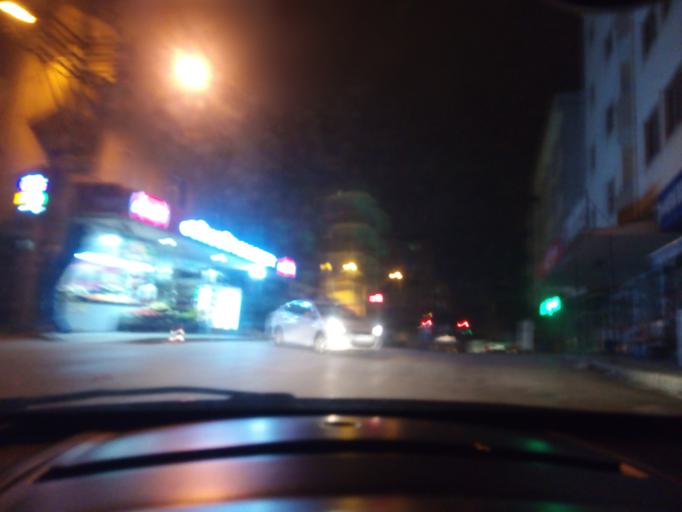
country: TR
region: Bursa
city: Niluefer
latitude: 40.2589
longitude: 28.9624
